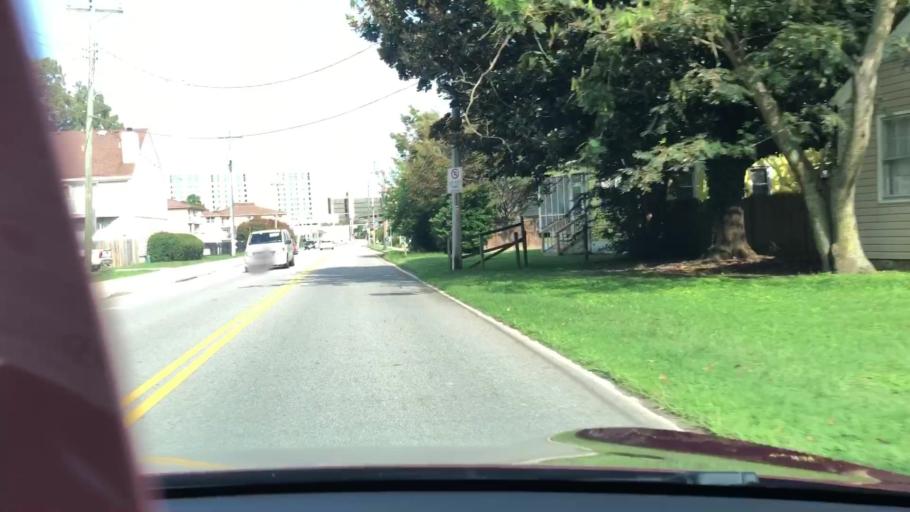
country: US
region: Virginia
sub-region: City of Virginia Beach
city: Virginia Beach
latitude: 36.8376
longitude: -75.9773
